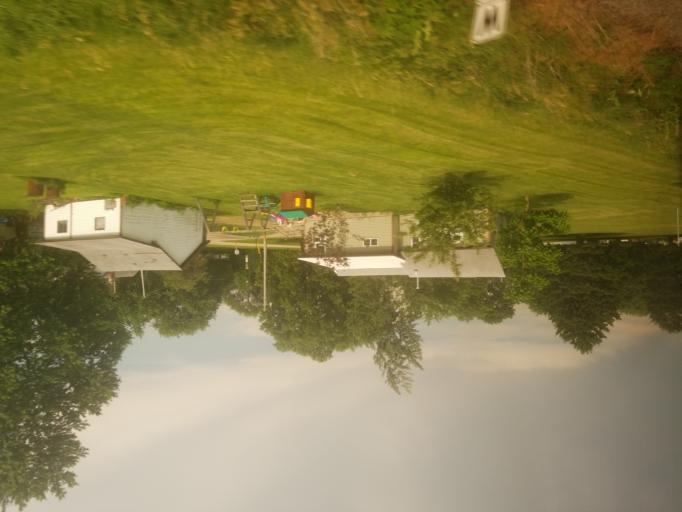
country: US
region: Illinois
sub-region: Bureau County
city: Princeton
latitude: 41.3625
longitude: -89.5881
